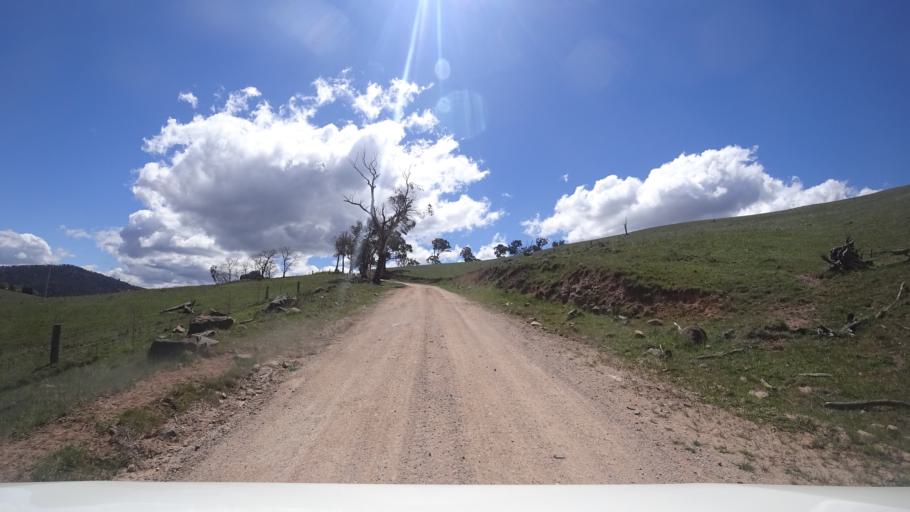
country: AU
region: New South Wales
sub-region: Oberon
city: Oberon
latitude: -33.5742
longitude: 149.9414
